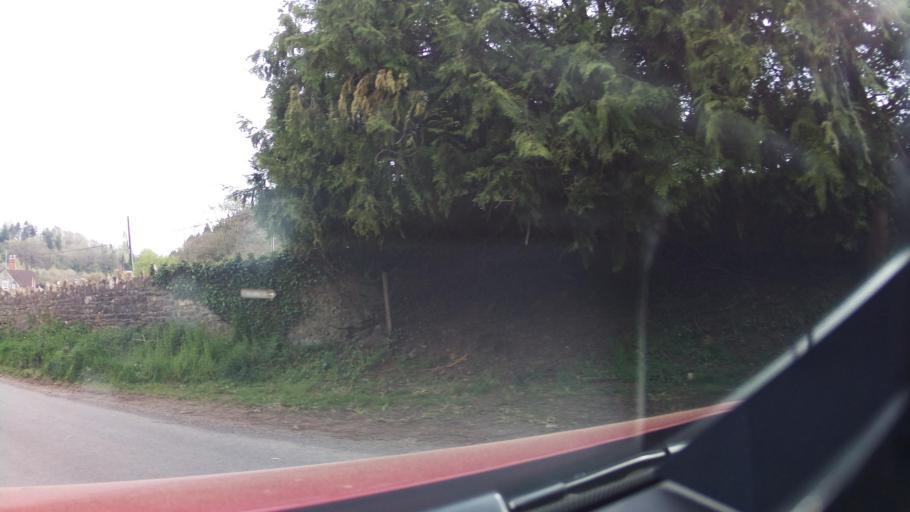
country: GB
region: England
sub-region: Somerset
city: Milborne Port
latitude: 50.9534
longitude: -2.4624
